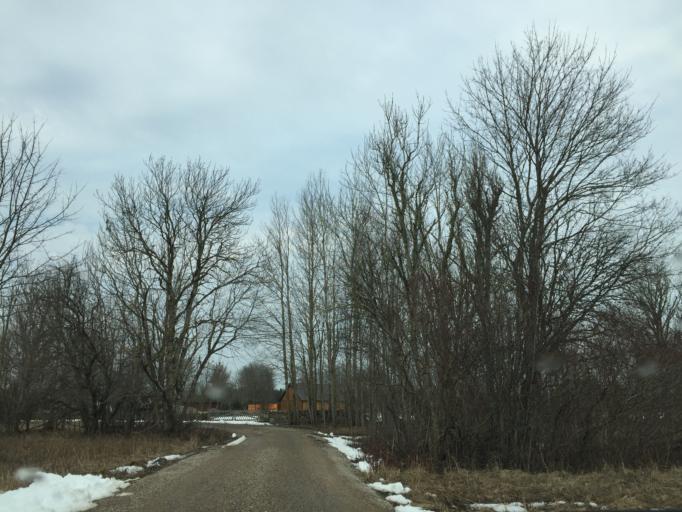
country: EE
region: Saare
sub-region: Kuressaare linn
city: Kuressaare
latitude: 58.4395
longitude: 22.1455
